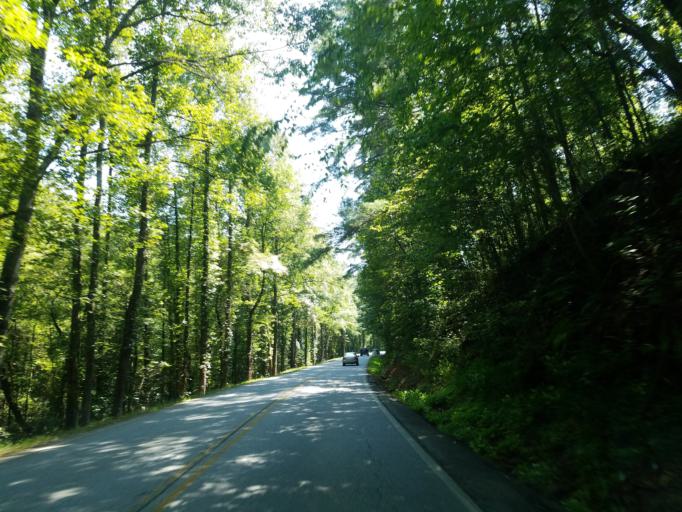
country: US
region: Georgia
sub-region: Lumpkin County
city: Dahlonega
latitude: 34.6307
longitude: -83.9356
